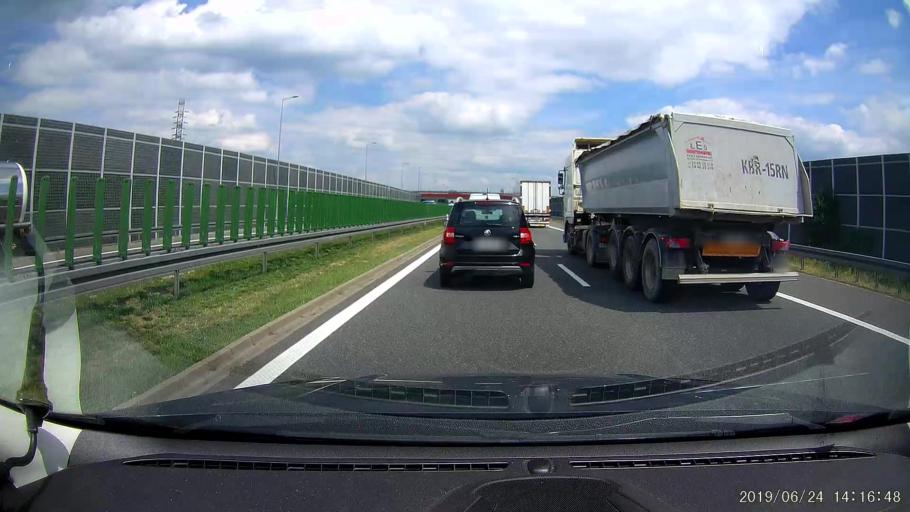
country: PL
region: Lesser Poland Voivodeship
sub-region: Powiat bochenski
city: Stanislawice
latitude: 49.9841
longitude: 20.3292
